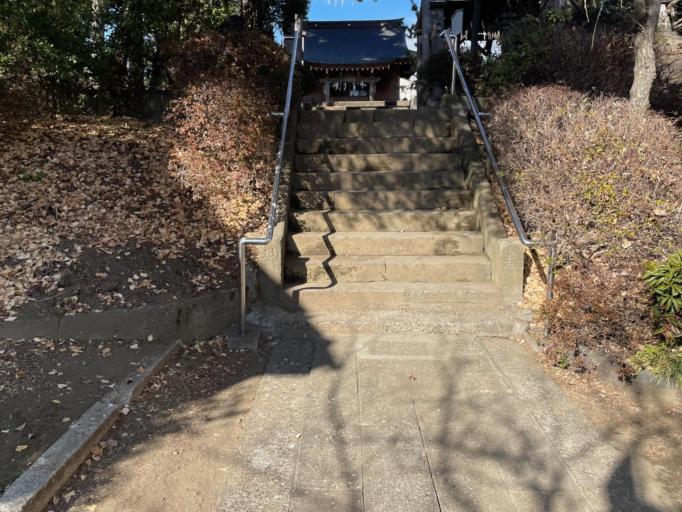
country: JP
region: Saitama
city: Wako
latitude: 35.7660
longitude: 139.6511
